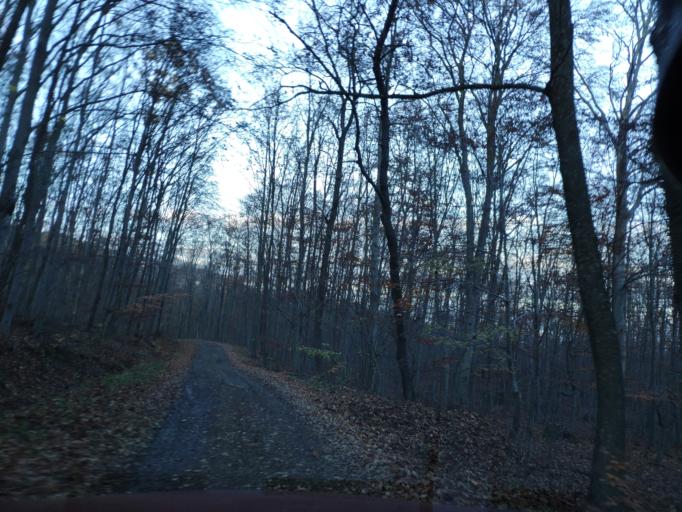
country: SK
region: Kosicky
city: Secovce
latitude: 48.5869
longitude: 21.5058
